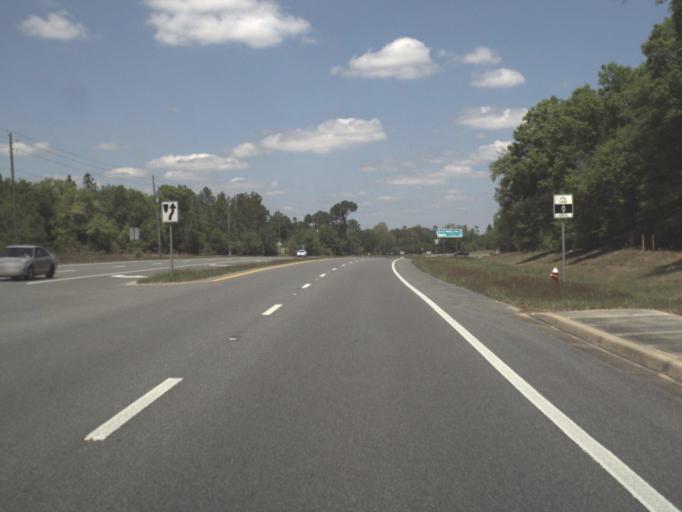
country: US
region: Florida
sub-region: Santa Rosa County
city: Point Baker
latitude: 30.6903
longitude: -87.0536
